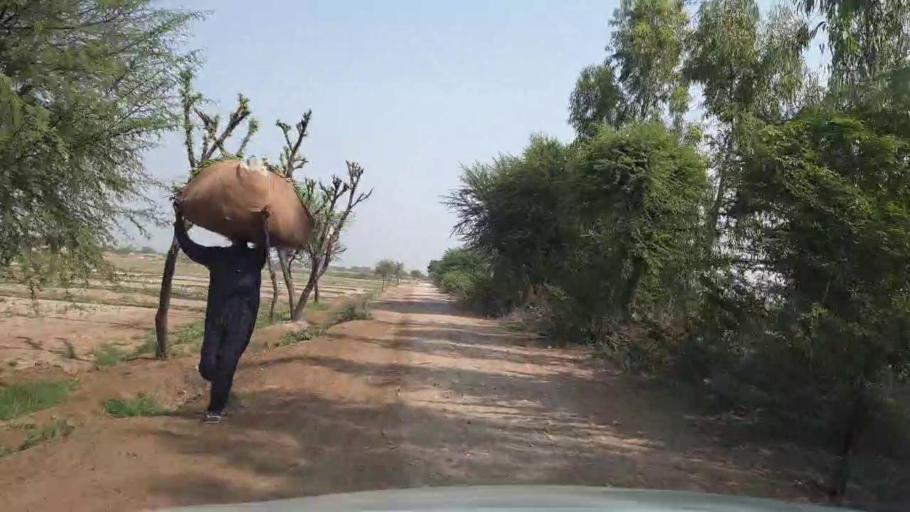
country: PK
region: Sindh
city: Chor
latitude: 25.4664
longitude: 69.7064
